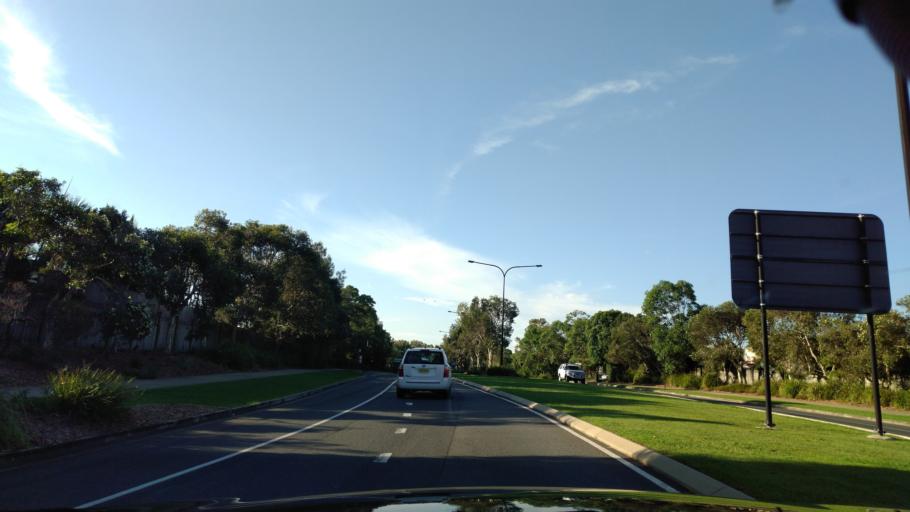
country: AU
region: Queensland
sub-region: Moreton Bay
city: Mango Hill
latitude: -27.2289
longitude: 153.0221
